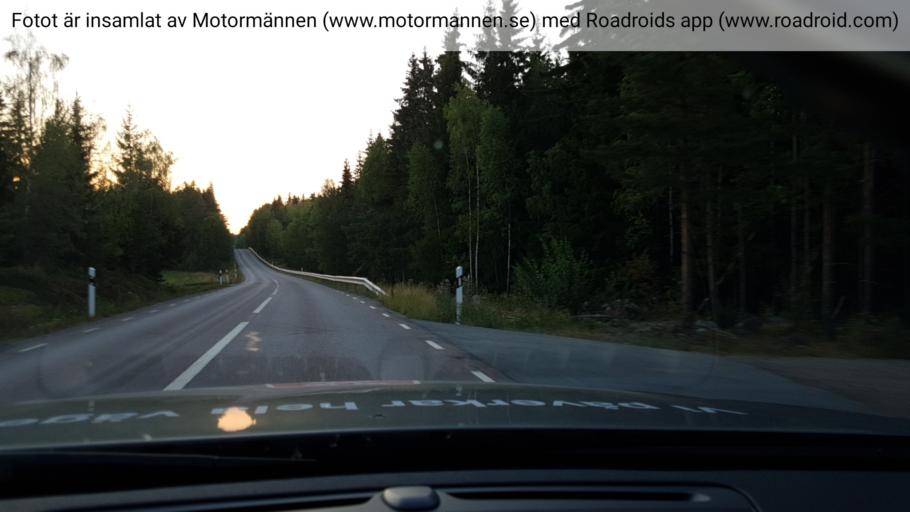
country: SE
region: Uppsala
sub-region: Osthammars Kommun
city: Bjorklinge
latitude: 59.9920
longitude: 17.3201
